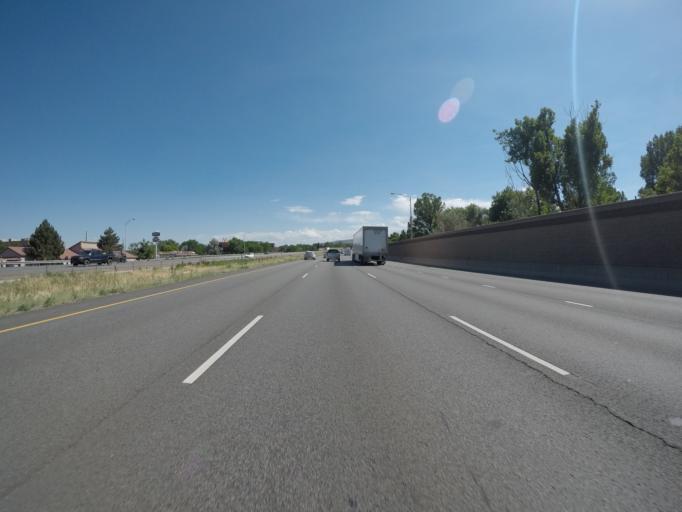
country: US
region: Colorado
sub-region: Jefferson County
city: Applewood
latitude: 39.7592
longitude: -105.1435
